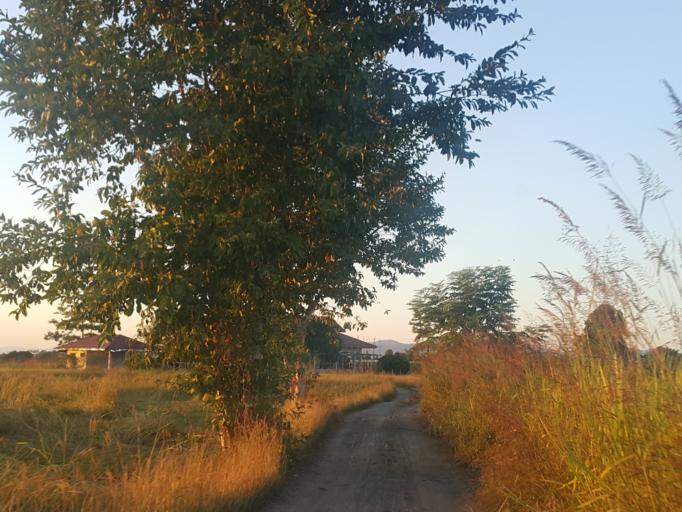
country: TH
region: Chiang Mai
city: San Kamphaeng
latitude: 18.8300
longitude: 99.1508
